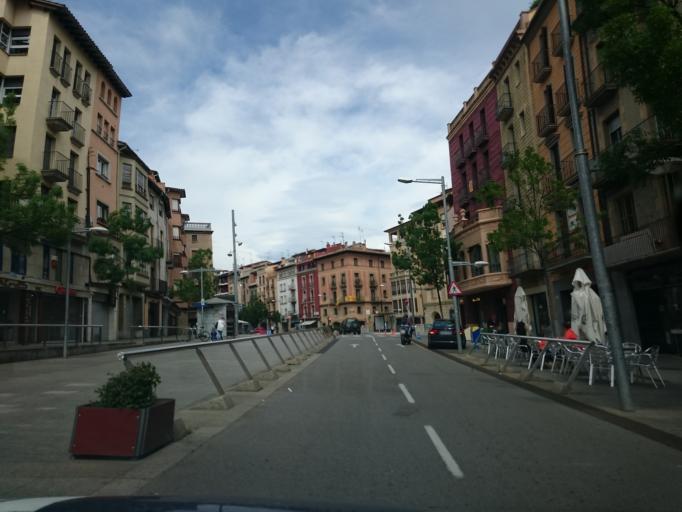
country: ES
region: Catalonia
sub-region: Provincia de Barcelona
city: Vic
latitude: 41.9307
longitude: 2.2559
